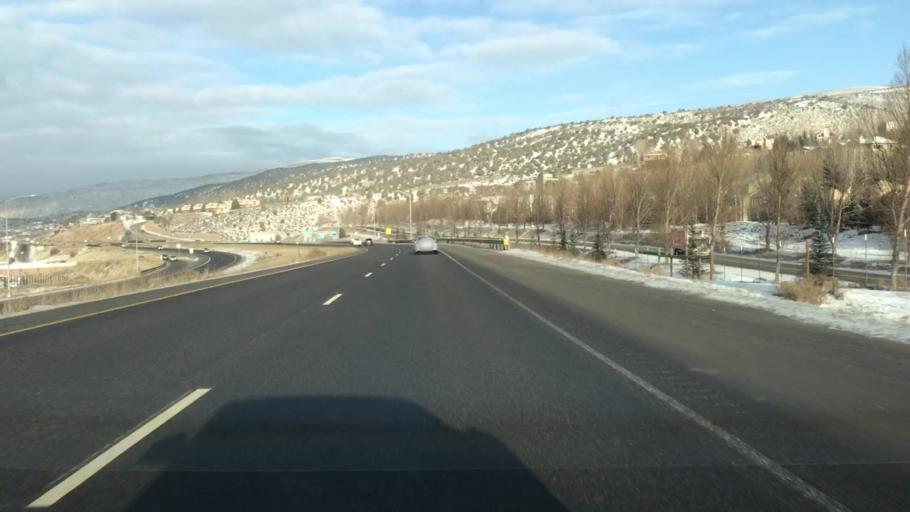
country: US
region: Colorado
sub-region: Eagle County
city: Edwards
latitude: 39.6467
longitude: -106.5819
